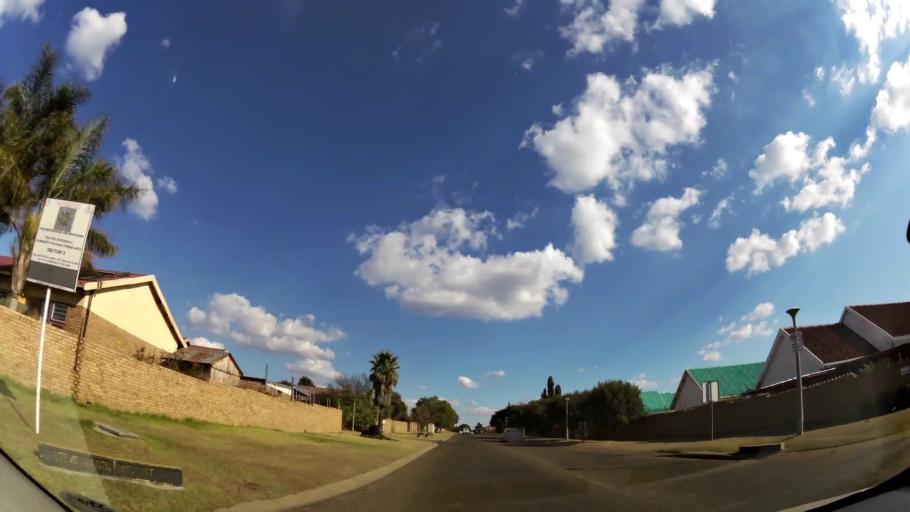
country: ZA
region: Mpumalanga
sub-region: Nkangala District Municipality
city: Witbank
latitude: -25.9005
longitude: 29.2459
